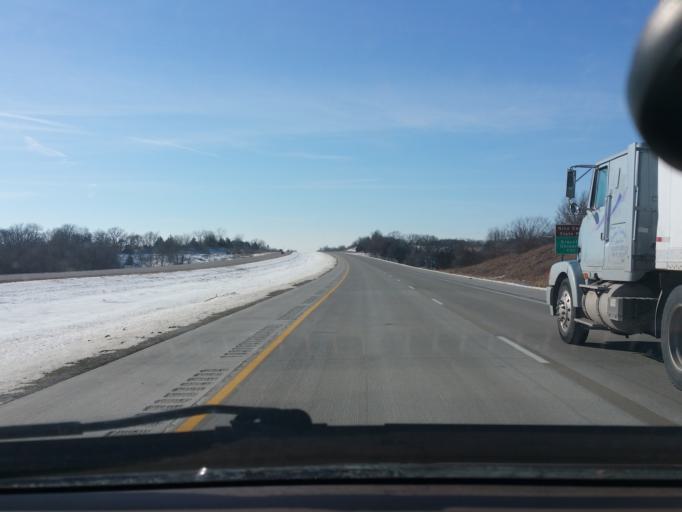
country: US
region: Iowa
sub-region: Decatur County
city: Lamoni
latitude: 40.6354
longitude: -93.8788
